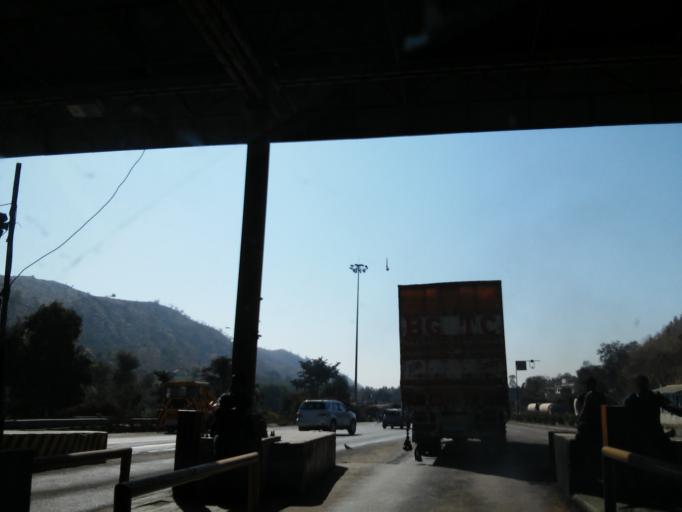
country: IN
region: Rajasthan
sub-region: Udaipur
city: Udaipur
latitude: 24.2716
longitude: 73.6740
